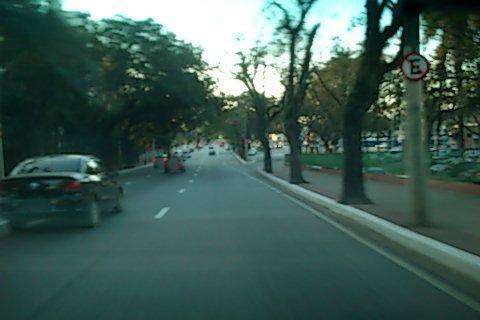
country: BR
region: Sao Paulo
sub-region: Sao Jose Dos Campos
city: Sao Jose dos Campos
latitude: -23.1725
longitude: -45.8901
